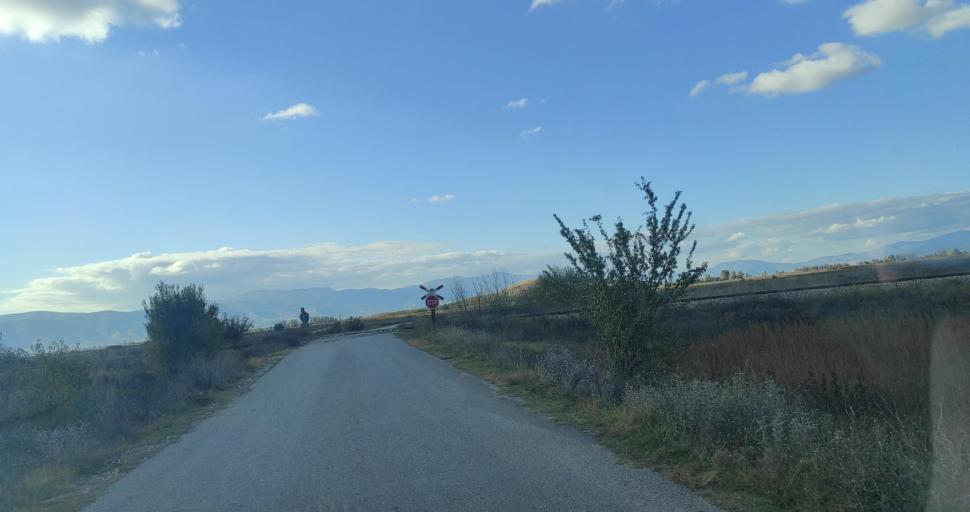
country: MK
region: Prilep
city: Topolcani
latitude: 41.2776
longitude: 21.4312
